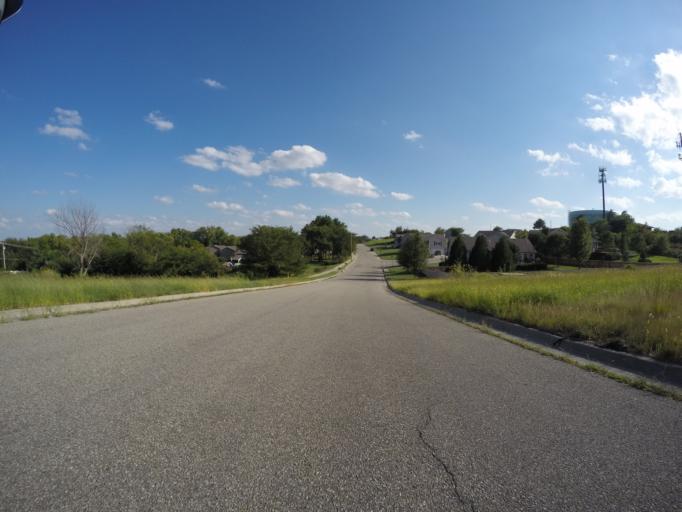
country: US
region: Kansas
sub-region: Riley County
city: Manhattan
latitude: 39.2112
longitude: -96.6274
